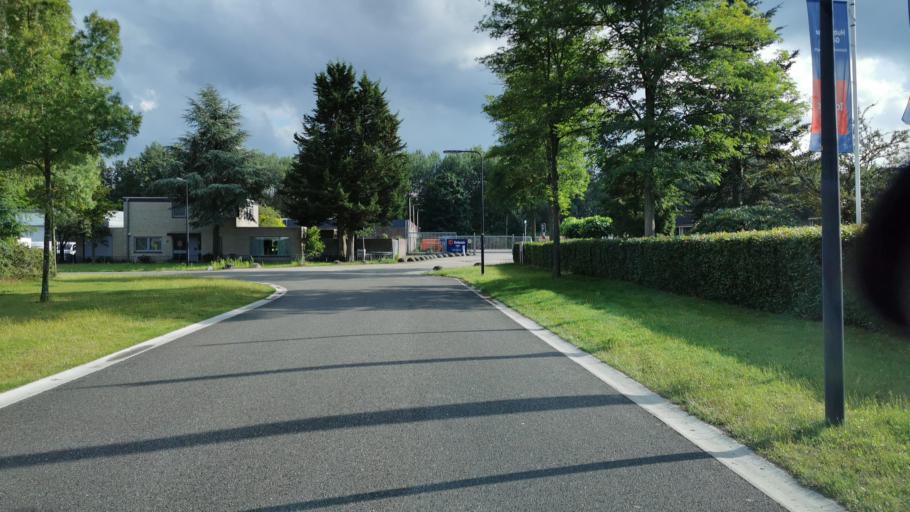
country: NL
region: Overijssel
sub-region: Gemeente Enschede
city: Enschede
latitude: 52.2230
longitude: 6.9489
